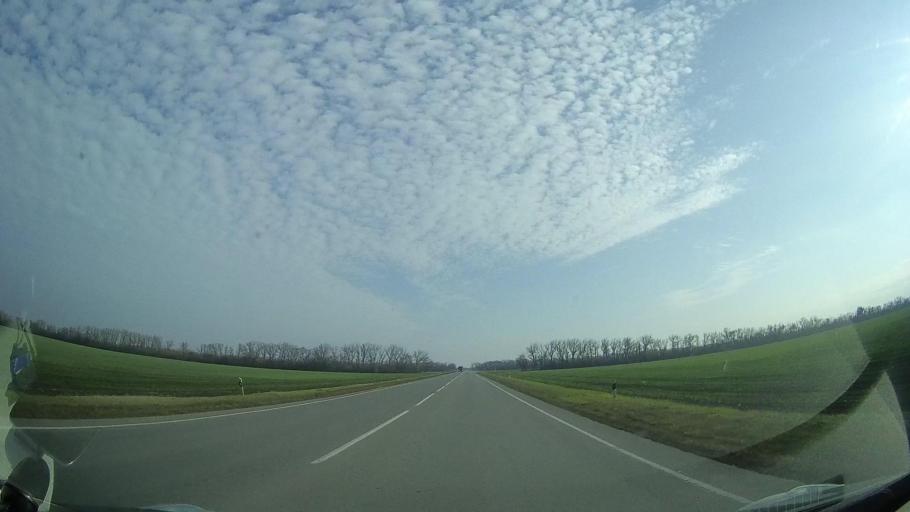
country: RU
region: Rostov
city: Tselina
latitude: 46.5237
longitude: 41.1185
